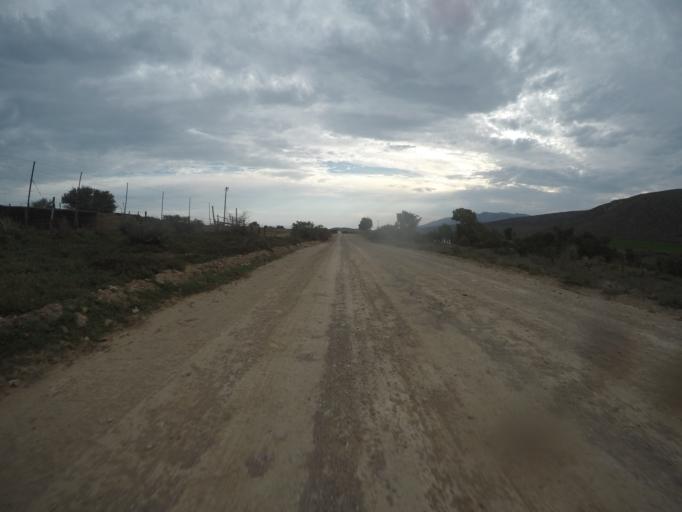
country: ZA
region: Eastern Cape
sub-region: Cacadu District Municipality
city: Willowmore
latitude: -33.4916
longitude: 23.5946
